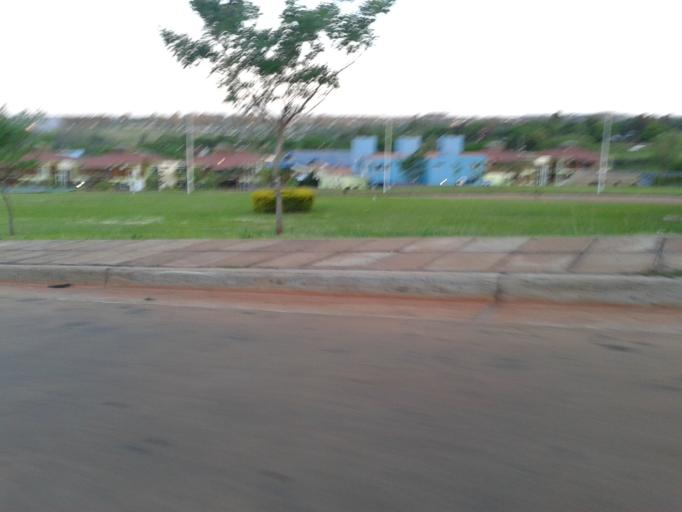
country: AR
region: Misiones
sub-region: Departamento de Capital
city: Posadas
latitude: -27.3962
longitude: -55.9633
